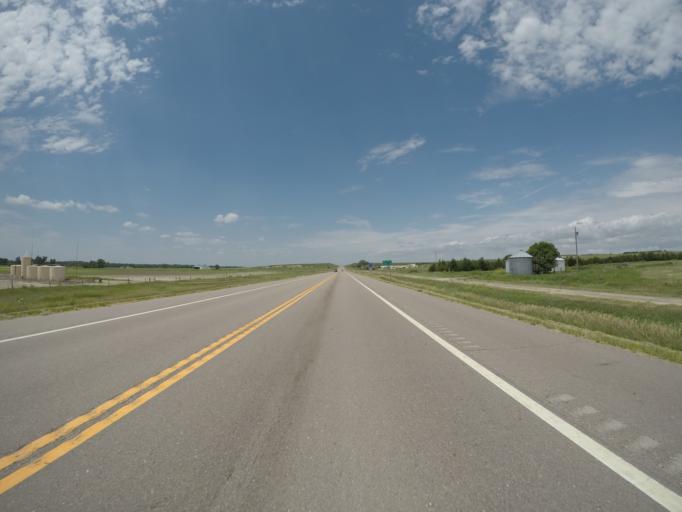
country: US
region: Kansas
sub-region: Graham County
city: Hill City
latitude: 39.3795
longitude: -99.6908
